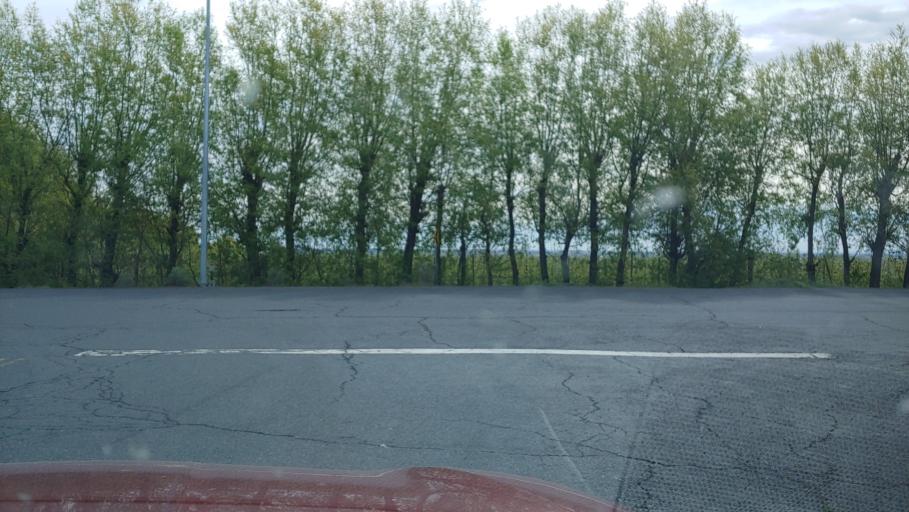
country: US
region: Washington
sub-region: Grant County
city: Quincy
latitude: 47.2325
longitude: -119.9539
